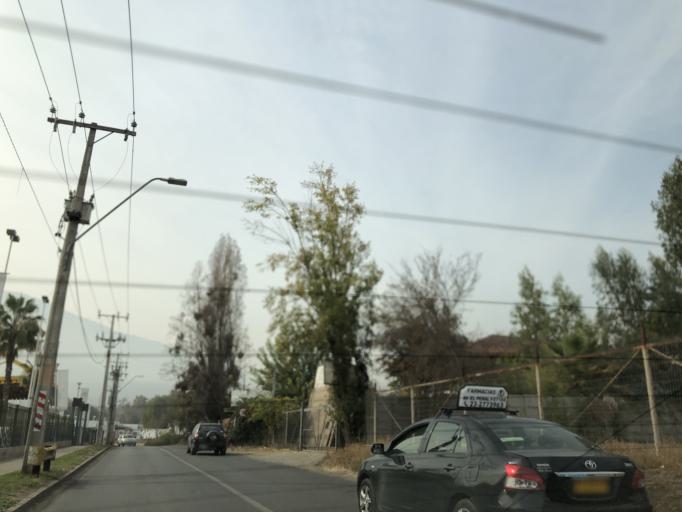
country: CL
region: Santiago Metropolitan
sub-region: Provincia de Cordillera
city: Puente Alto
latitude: -33.5717
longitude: -70.5576
